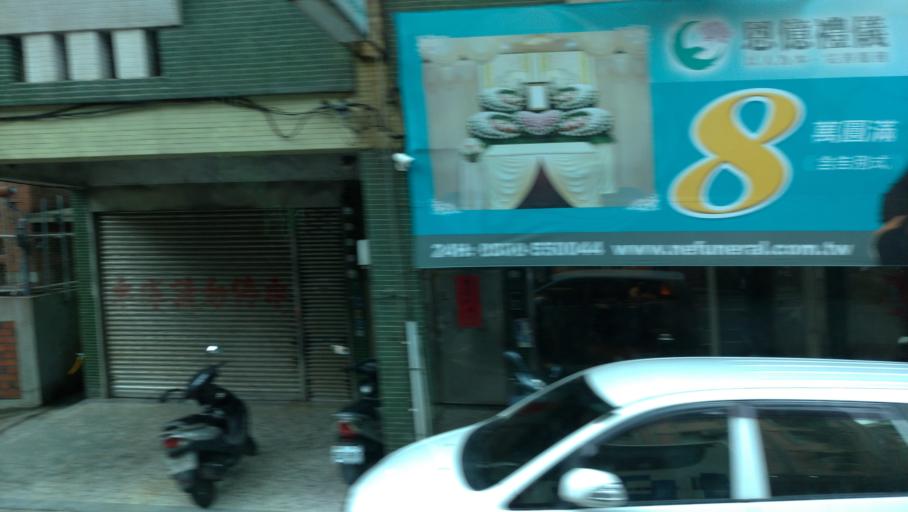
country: TW
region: Taiwan
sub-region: Keelung
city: Keelung
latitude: 25.1465
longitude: 121.7614
